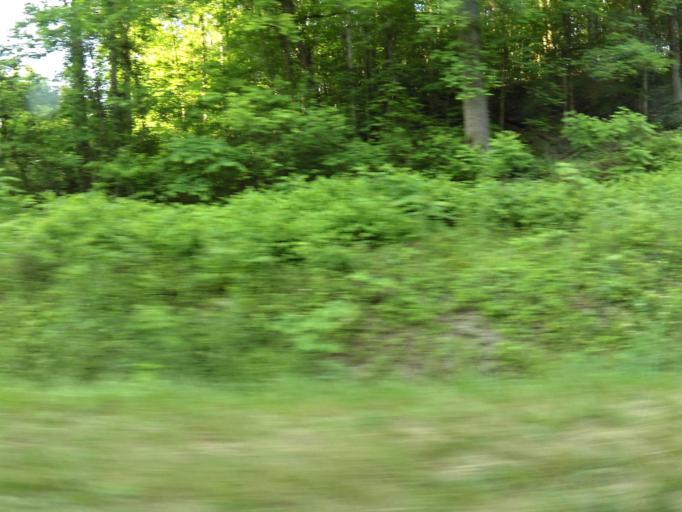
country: US
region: Tennessee
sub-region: Sevier County
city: Seymour
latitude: 35.8505
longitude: -83.7132
